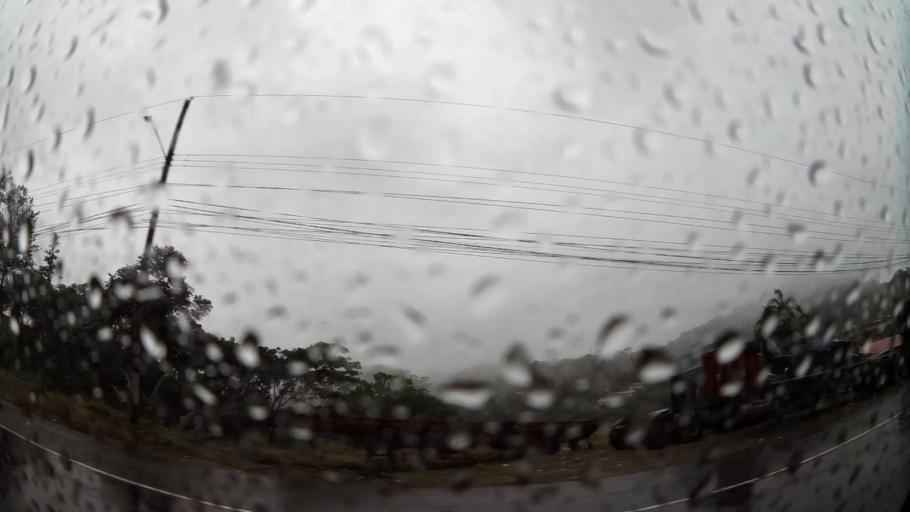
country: PA
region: Colon
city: Gatun
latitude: 9.2899
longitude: -79.7471
